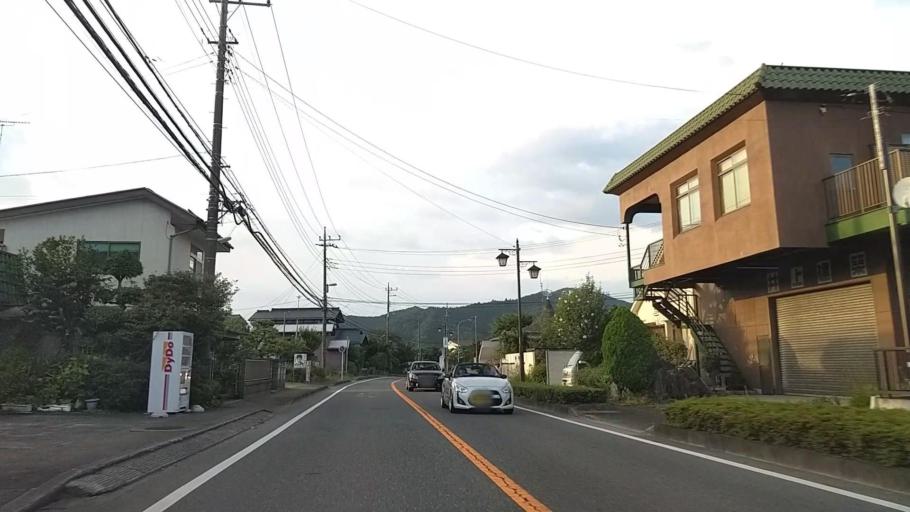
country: JP
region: Yamanashi
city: Uenohara
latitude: 35.5213
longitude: 139.2311
